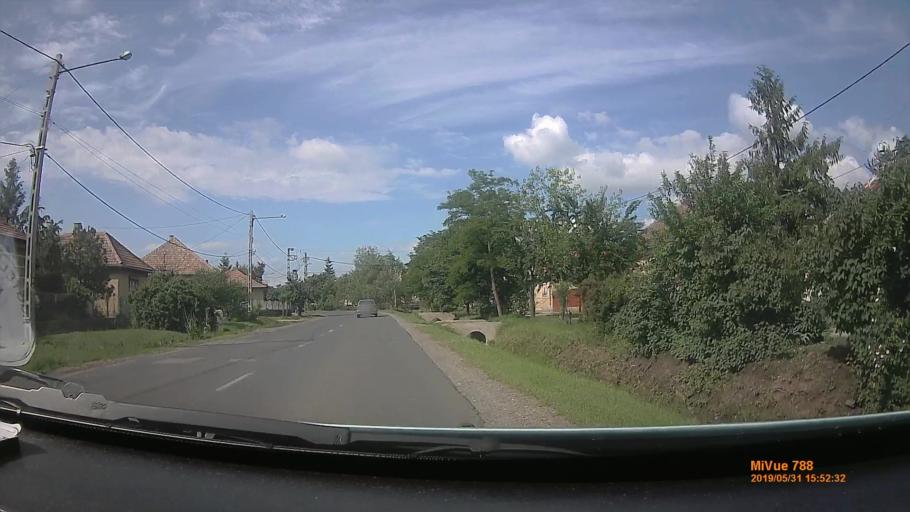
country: HU
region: Borsod-Abauj-Zemplen
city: Szerencs
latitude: 48.1521
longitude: 21.2017
